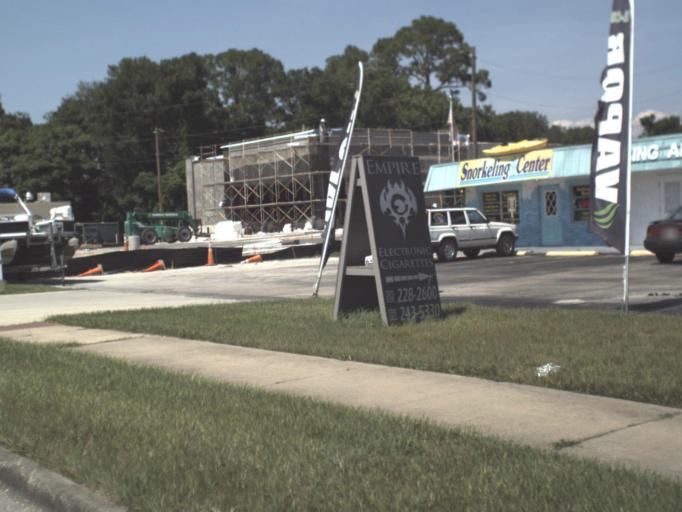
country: US
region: Florida
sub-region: Citrus County
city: Homosassa Springs
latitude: 28.8013
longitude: -82.5763
